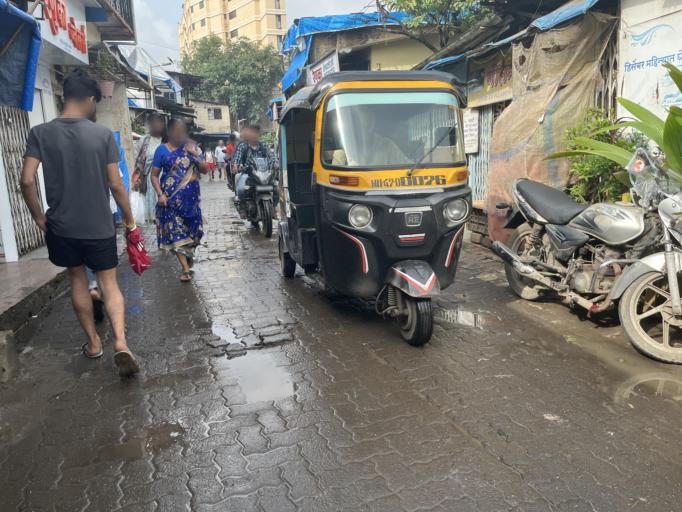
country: IN
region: Maharashtra
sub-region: Mumbai Suburban
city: Borivli
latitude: 19.2356
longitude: 72.8669
